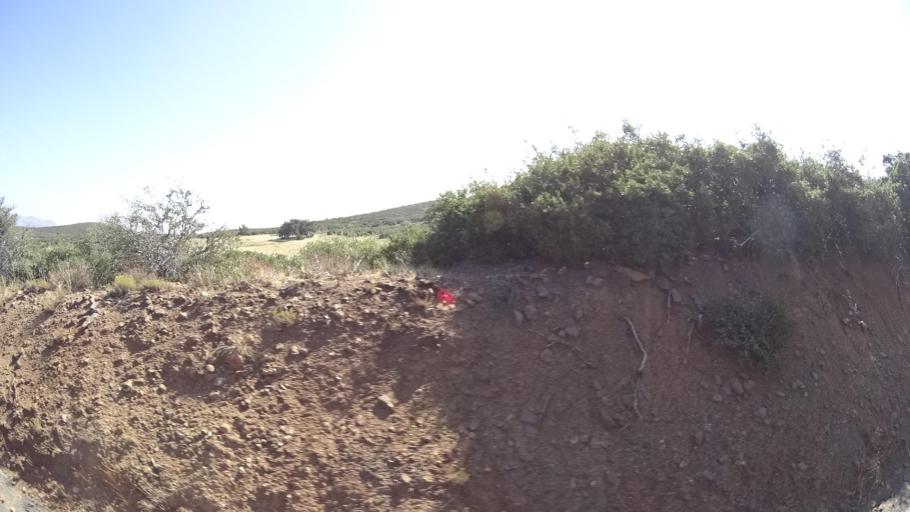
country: US
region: California
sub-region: San Diego County
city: Julian
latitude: 32.9861
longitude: -116.5331
